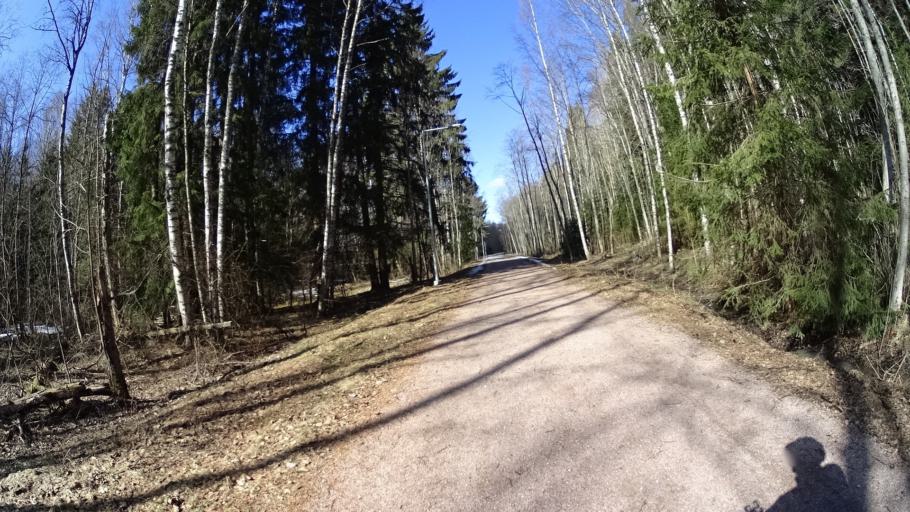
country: FI
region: Uusimaa
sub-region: Helsinki
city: Espoo
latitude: 60.1851
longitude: 24.6826
